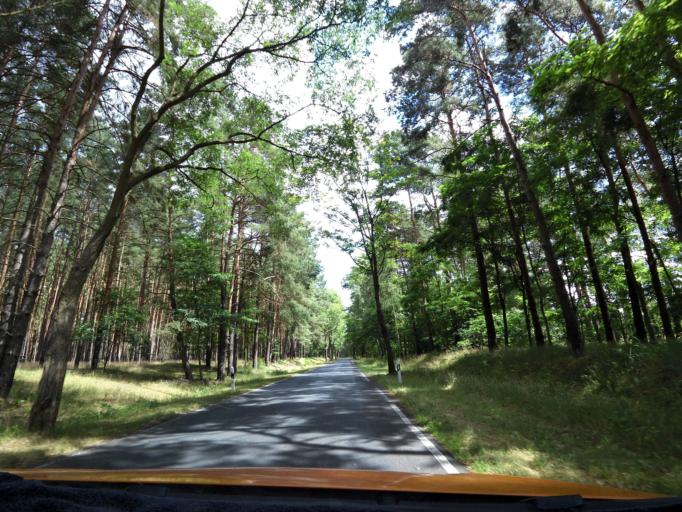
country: DE
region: Brandenburg
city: Storkow
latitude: 52.2457
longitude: 13.8418
